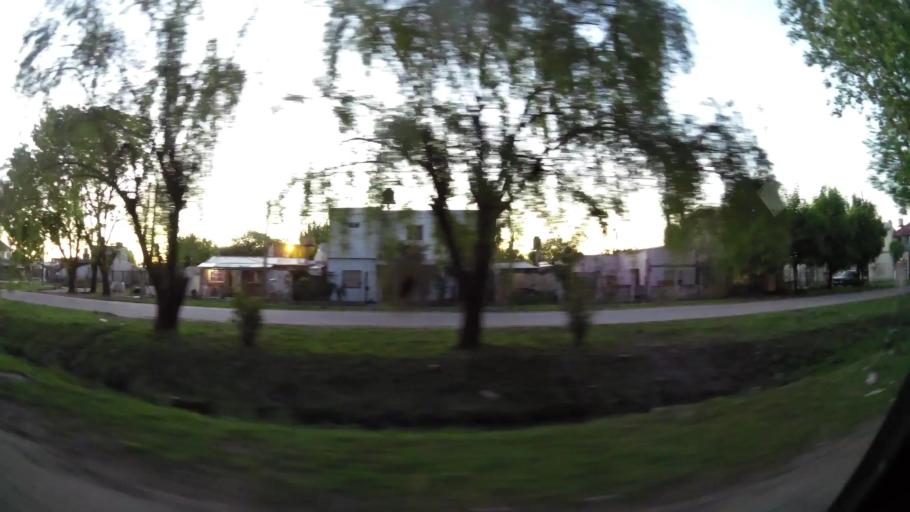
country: AR
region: Buenos Aires
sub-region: Partido de Almirante Brown
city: Adrogue
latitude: -34.7835
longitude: -58.3238
